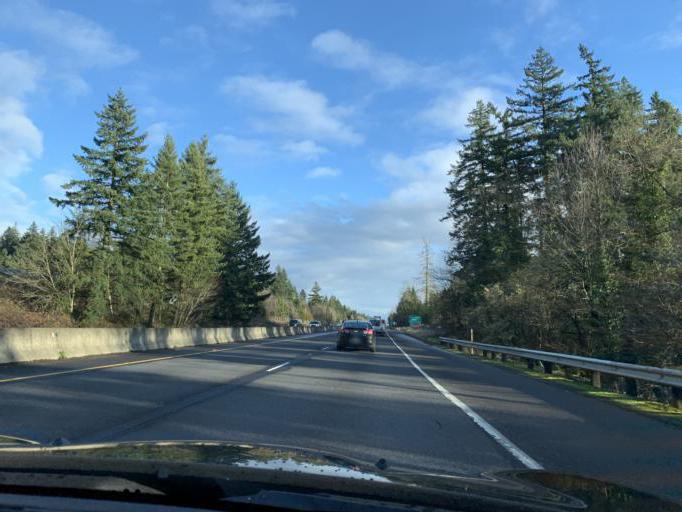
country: US
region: Washington
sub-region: Clark County
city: Orchards
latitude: 45.6092
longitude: -122.5767
